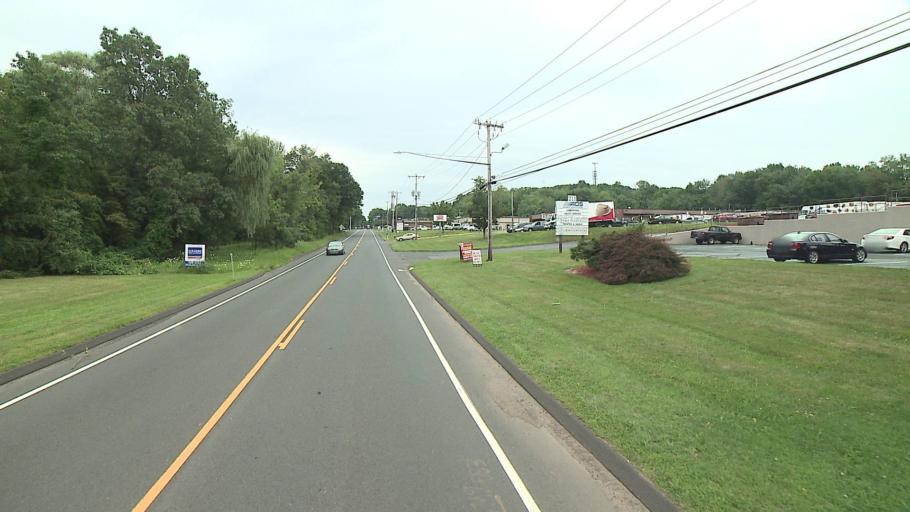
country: US
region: Connecticut
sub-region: Middlesex County
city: Cromwell
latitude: 41.6285
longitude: -72.6769
